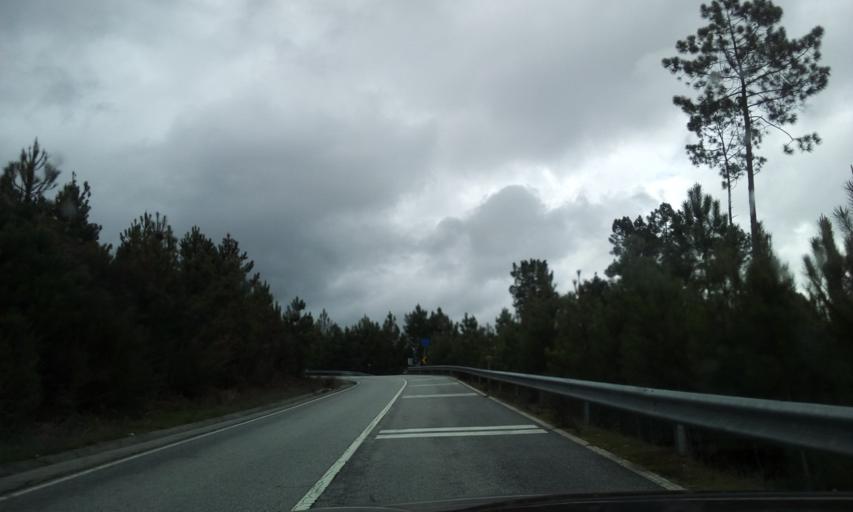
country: PT
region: Viseu
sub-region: Viseu
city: Rio de Loba
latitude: 40.6172
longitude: -7.8645
